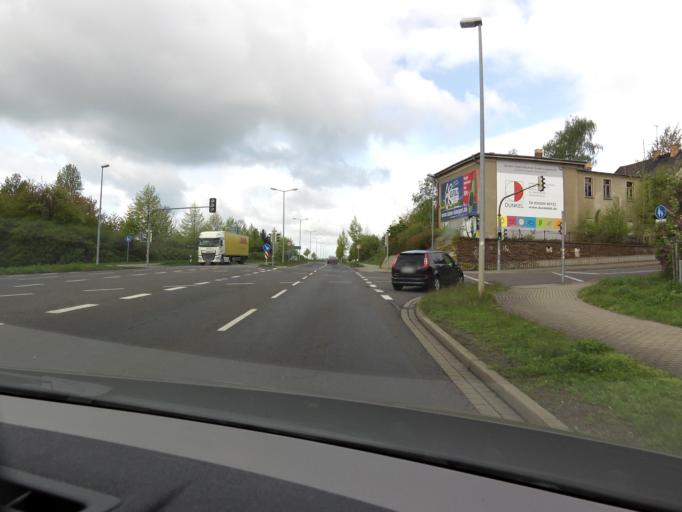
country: DE
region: Saxony
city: Schkeuditz
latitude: 51.4030
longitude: 12.2212
